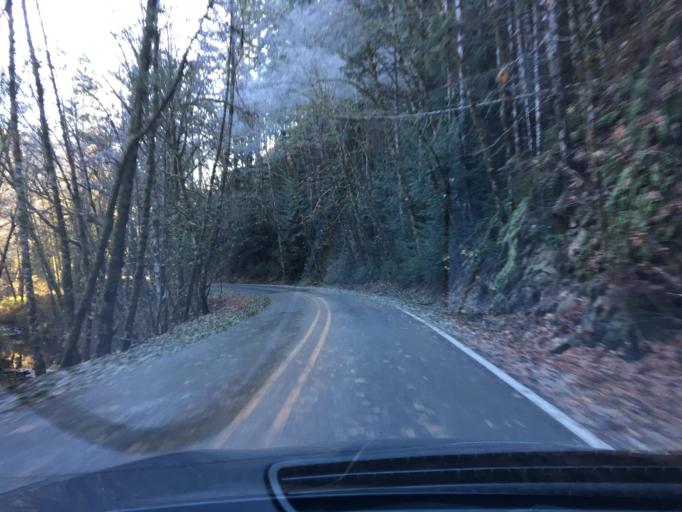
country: US
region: Oregon
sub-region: Douglas County
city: Roseburg
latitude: 43.3269
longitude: -123.5862
